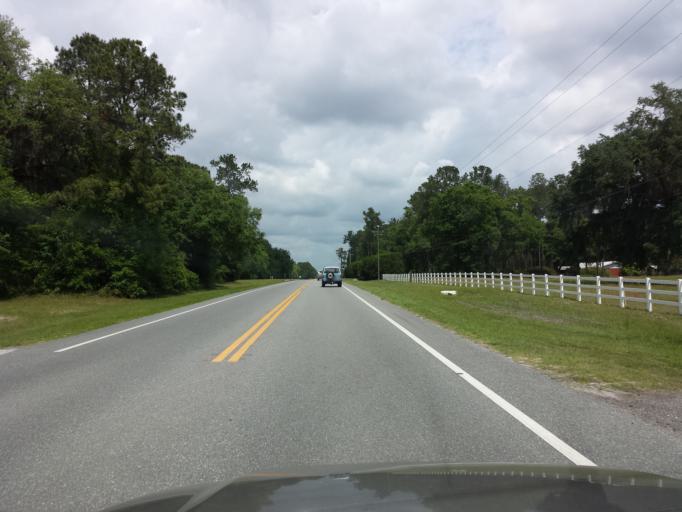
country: US
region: Florida
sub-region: Columbia County
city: Watertown
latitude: 30.0511
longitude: -82.5988
